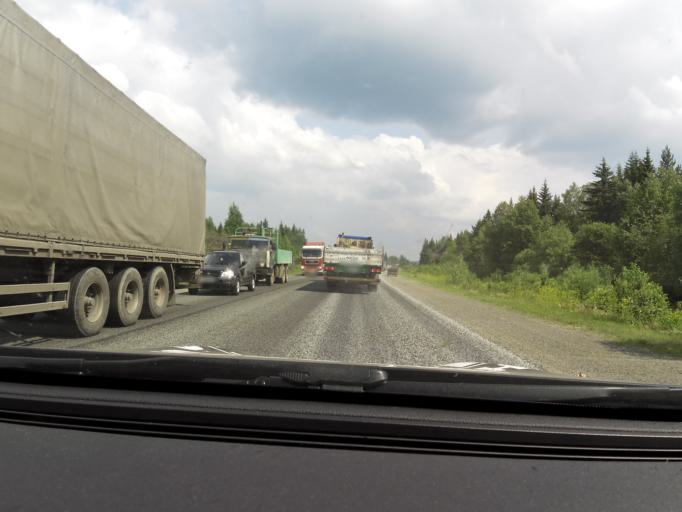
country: RU
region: Sverdlovsk
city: Ufimskiy
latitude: 56.7712
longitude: 58.1145
